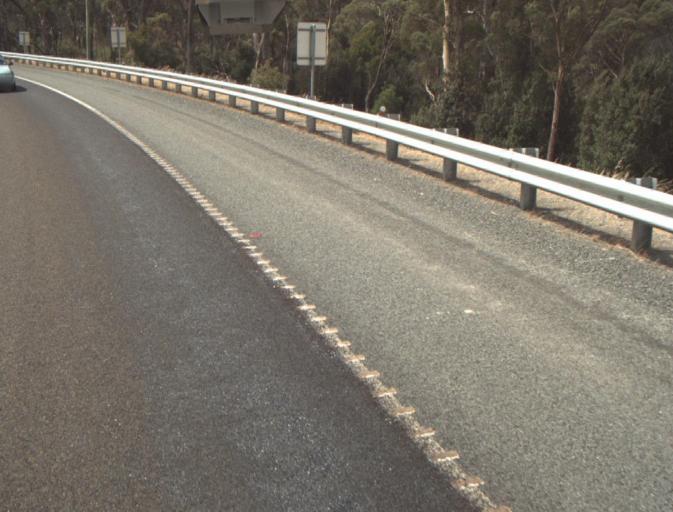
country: AU
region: Tasmania
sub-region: Launceston
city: Mayfield
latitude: -41.2977
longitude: 147.0497
